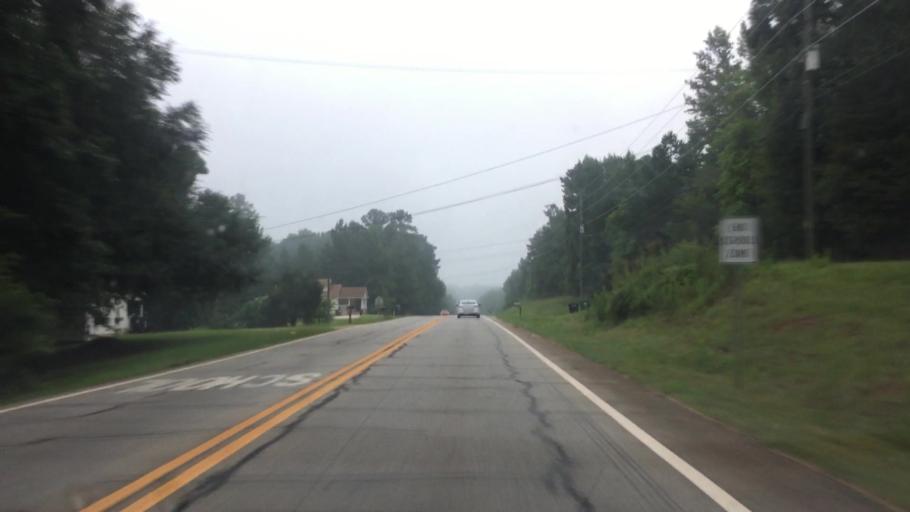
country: US
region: Georgia
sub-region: Henry County
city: Stockbridge
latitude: 33.5524
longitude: -84.1376
